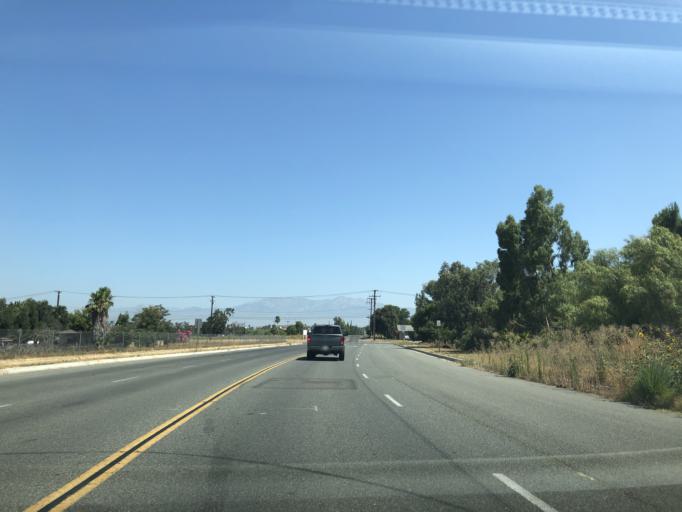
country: US
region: California
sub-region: Riverside County
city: Corona
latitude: 33.9007
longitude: -117.5668
